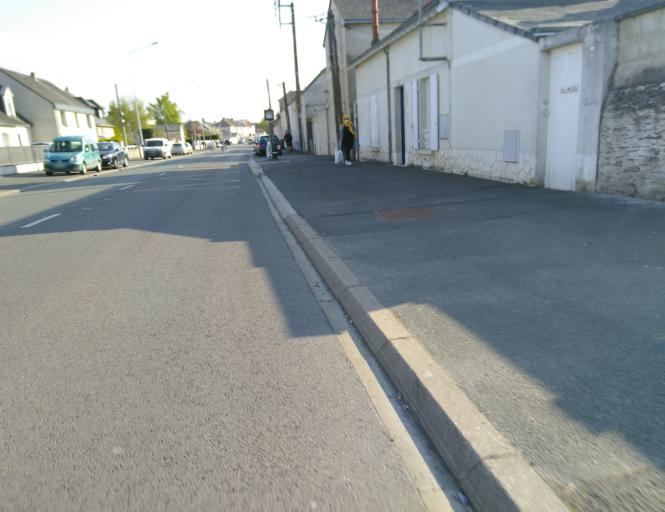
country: FR
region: Pays de la Loire
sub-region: Departement de Maine-et-Loire
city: Angers
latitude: 47.4629
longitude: -0.5197
